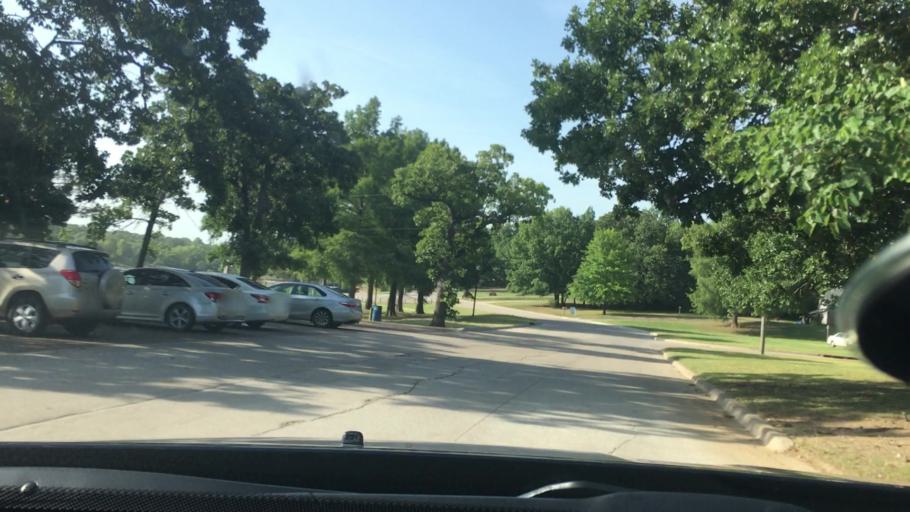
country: US
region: Oklahoma
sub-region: Pontotoc County
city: Ada
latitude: 34.7652
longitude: -96.6563
